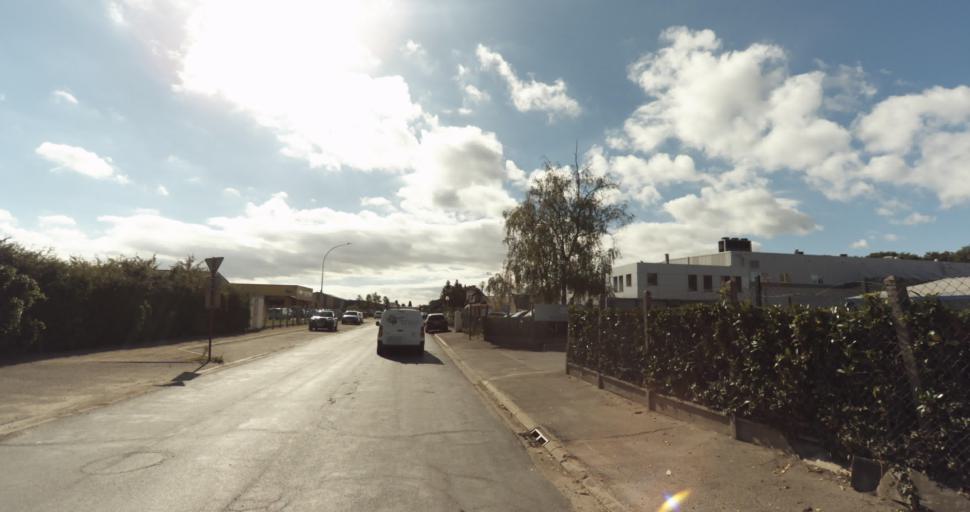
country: FR
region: Centre
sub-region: Departement d'Eure-et-Loir
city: Garnay
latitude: 48.7312
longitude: 1.3214
